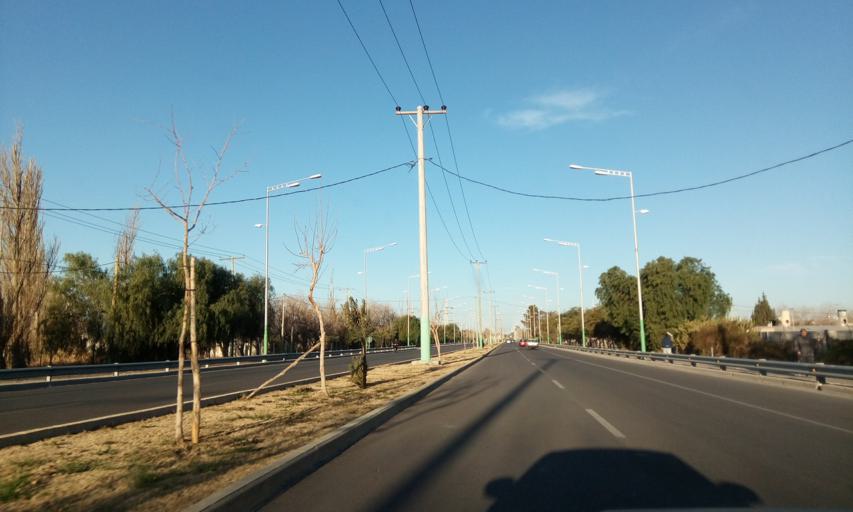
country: AR
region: San Juan
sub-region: Departamento de Rivadavia
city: Rivadavia
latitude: -31.5276
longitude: -68.6065
